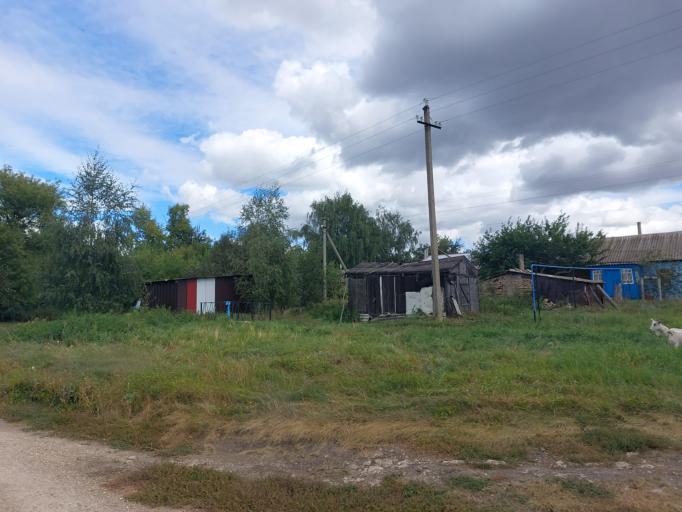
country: RU
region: Lipetsk
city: Terbuny
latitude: 52.2621
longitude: 38.2068
